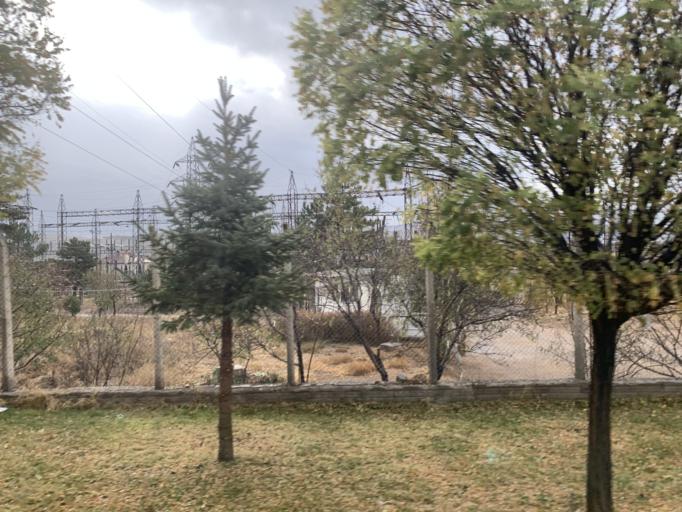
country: TR
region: Nevsehir
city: Avanos
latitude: 38.7211
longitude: 34.8592
